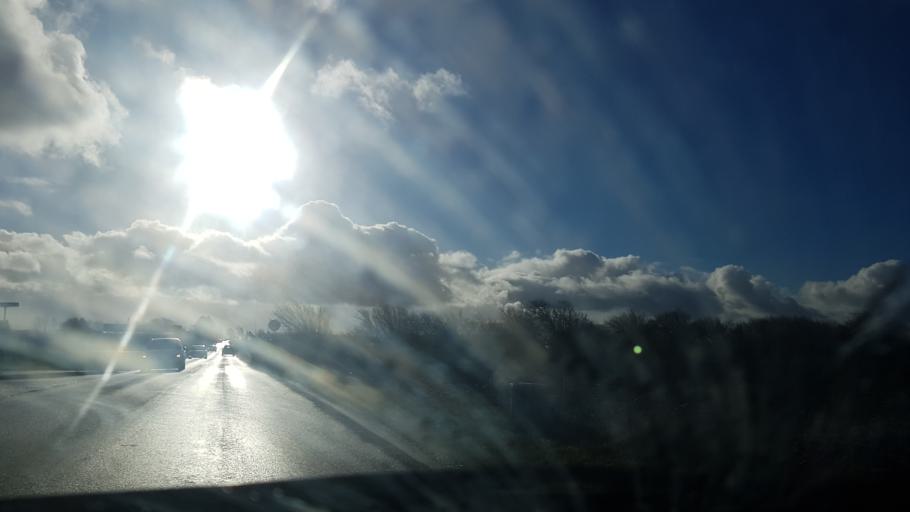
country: DK
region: South Denmark
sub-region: Fredericia Kommune
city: Taulov
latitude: 55.5238
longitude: 9.6376
